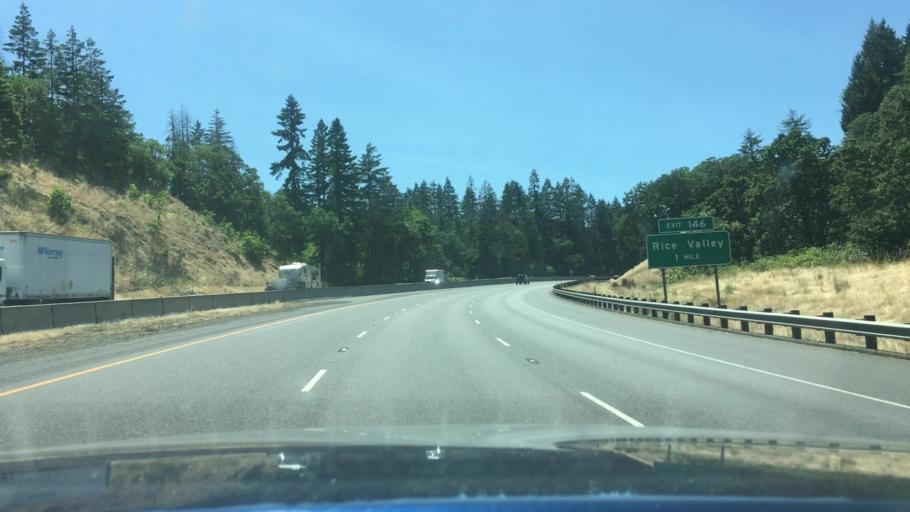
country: US
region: Oregon
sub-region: Douglas County
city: Yoncalla
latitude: 43.5285
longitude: -123.3025
